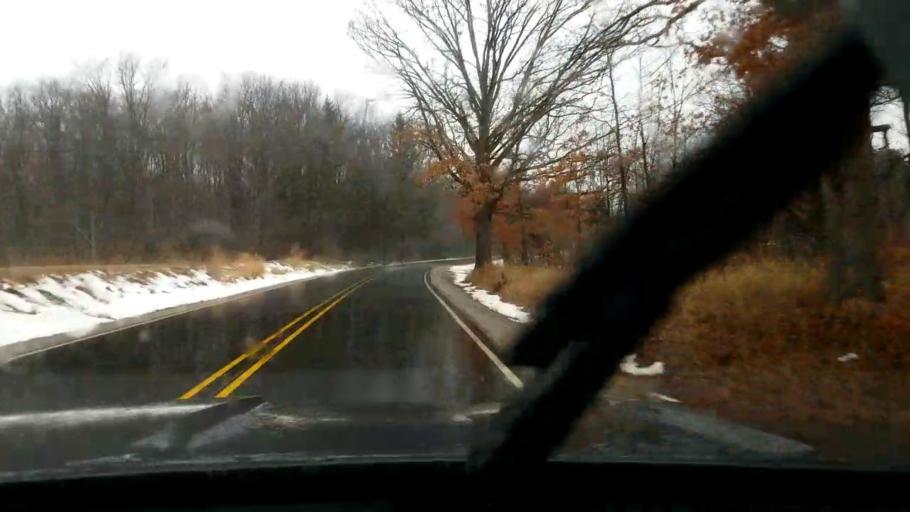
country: US
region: Michigan
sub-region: Jackson County
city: Grass Lake
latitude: 42.3280
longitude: -84.1965
